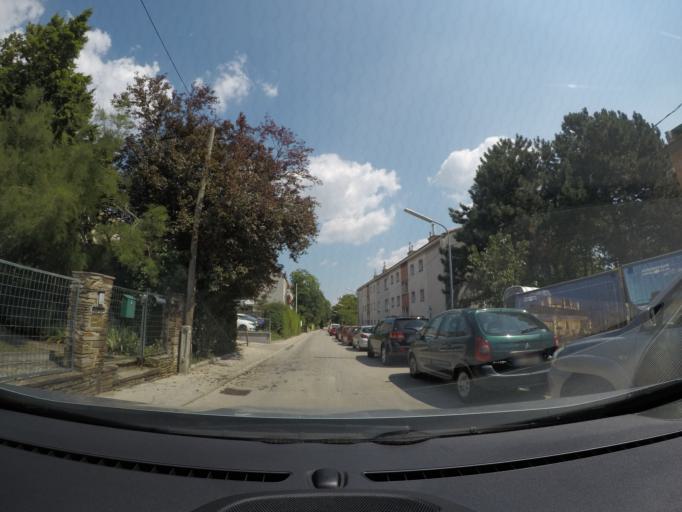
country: AT
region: Lower Austria
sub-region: Politischer Bezirk Wien-Umgebung
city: Purkersdorf
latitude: 48.2063
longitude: 16.2496
